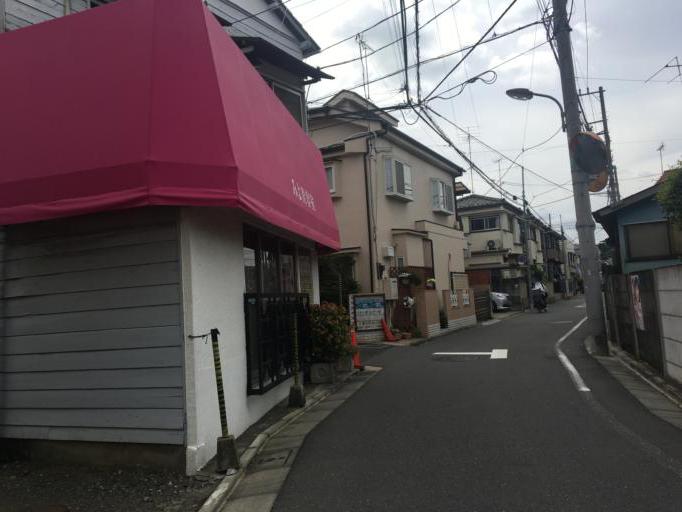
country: JP
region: Saitama
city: Wako
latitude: 35.7426
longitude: 139.6611
